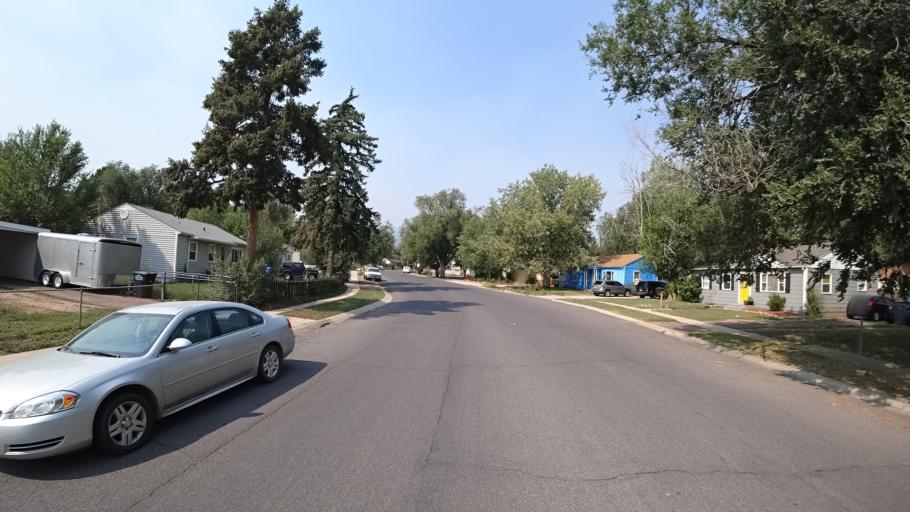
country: US
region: Colorado
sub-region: El Paso County
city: Colorado Springs
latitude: 38.8036
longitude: -104.8132
